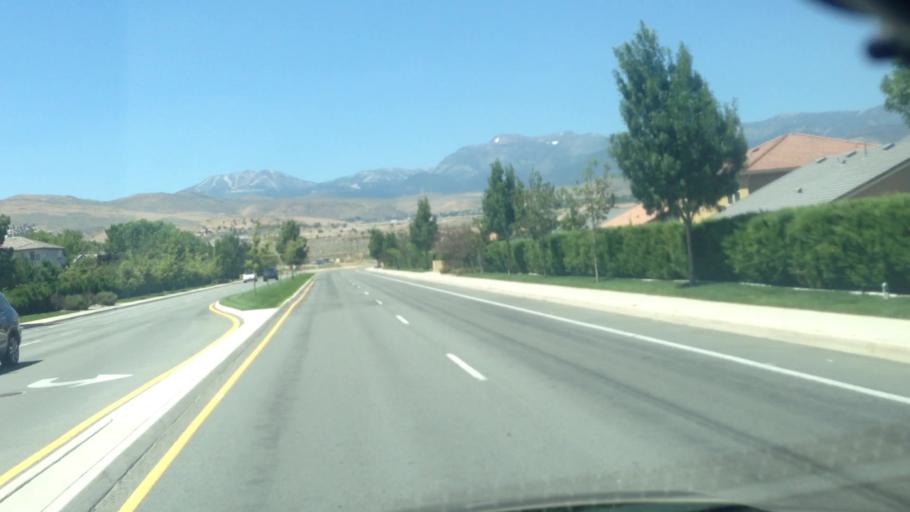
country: US
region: Nevada
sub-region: Storey County
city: Virginia City
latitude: 39.4044
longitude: -119.7368
